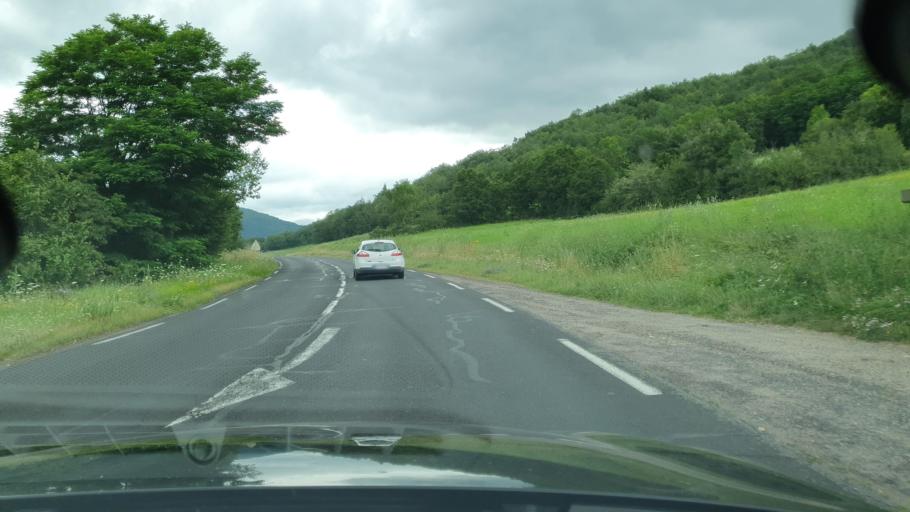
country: FR
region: Auvergne
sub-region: Departement du Puy-de-Dome
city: Champeix
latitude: 45.5734
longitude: 3.0352
